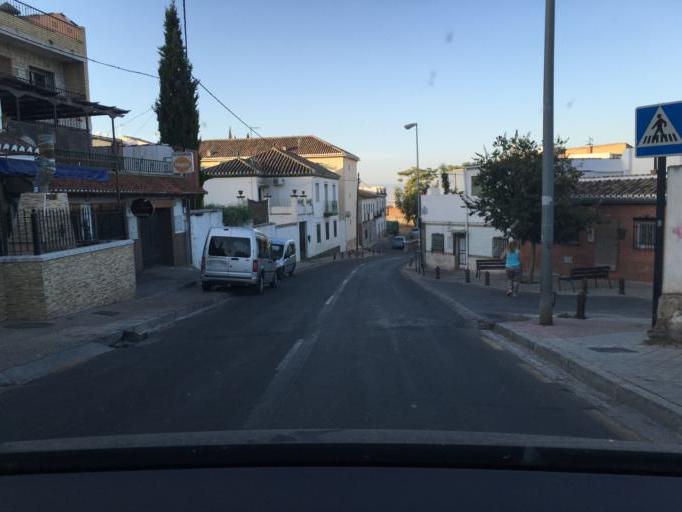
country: ES
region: Andalusia
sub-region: Provincia de Granada
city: Granada
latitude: 37.1882
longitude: -3.5903
